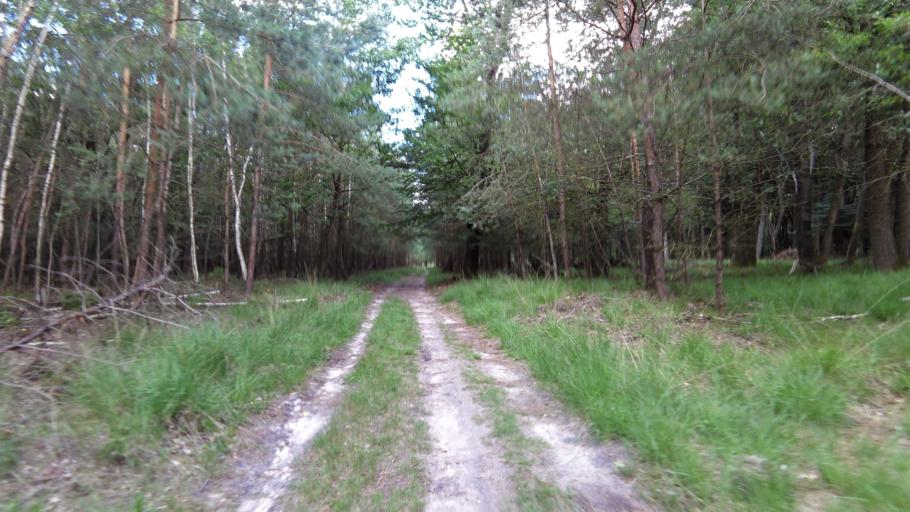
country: NL
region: Gelderland
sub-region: Gemeente Apeldoorn
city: Uddel
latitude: 52.2568
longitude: 5.8221
